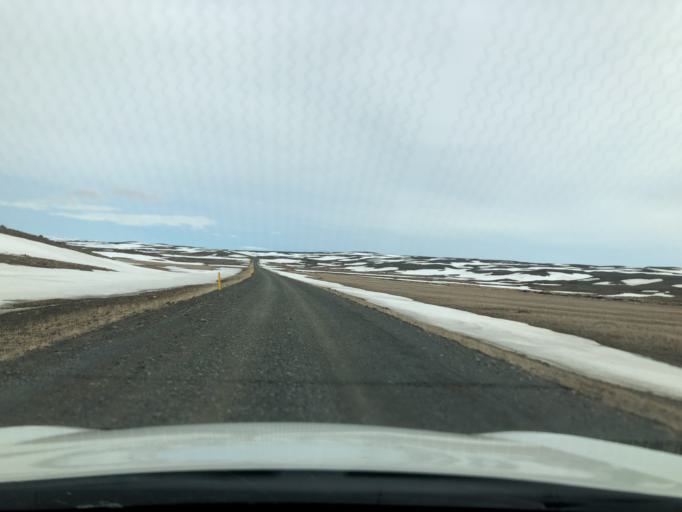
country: IS
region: East
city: Egilsstadir
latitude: 65.2972
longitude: -15.4252
